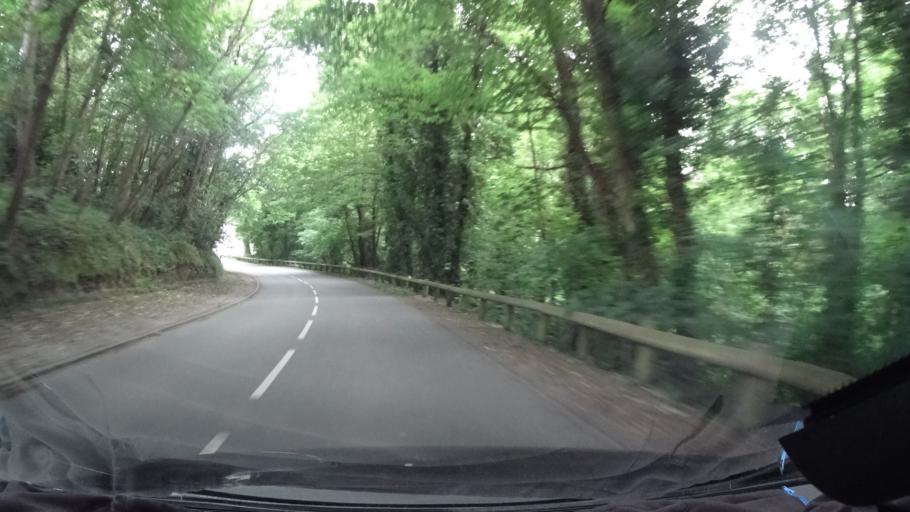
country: FR
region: Brittany
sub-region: Departement d'Ille-et-Vilaine
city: Le Minihic-sur-Rance
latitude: 48.5735
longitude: -2.0172
